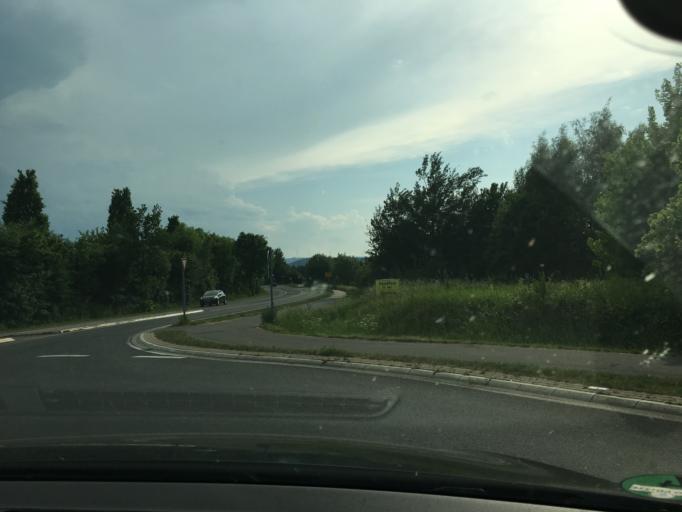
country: DE
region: North Rhine-Westphalia
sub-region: Regierungsbezirk Koln
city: Nideggen
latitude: 50.6969
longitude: 6.4885
